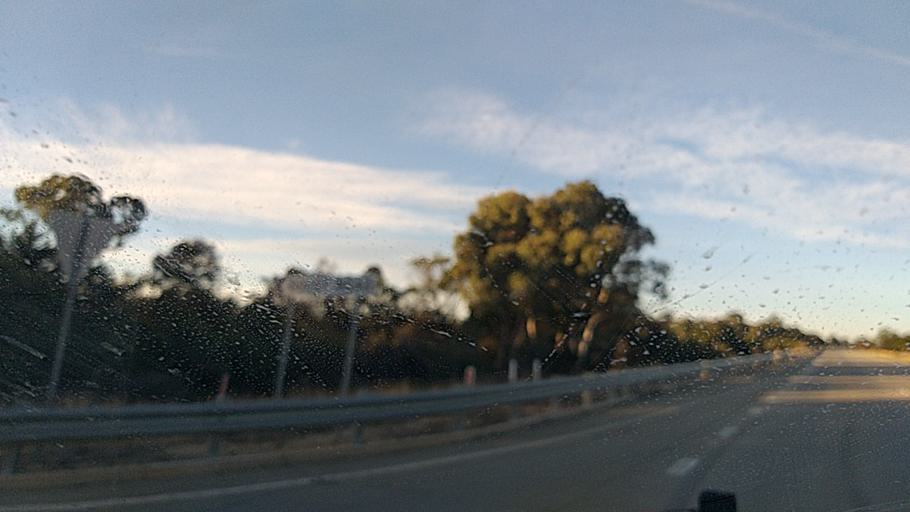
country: AU
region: New South Wales
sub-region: Yass Valley
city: Gundaroo
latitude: -35.1269
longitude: 149.3428
